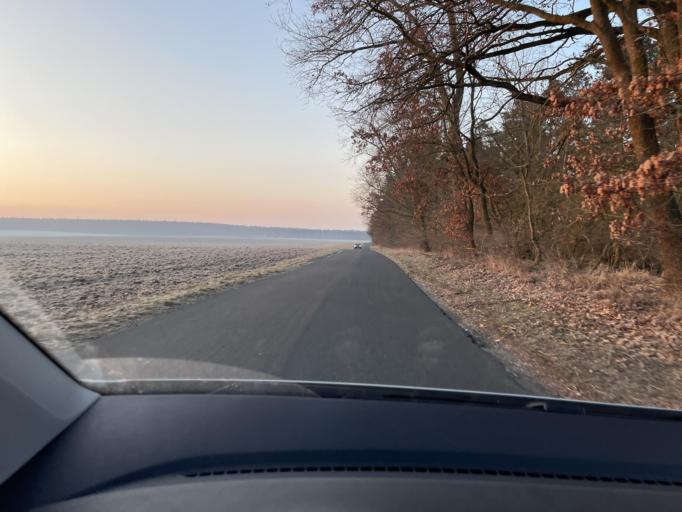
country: DE
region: Brandenburg
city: Roskow
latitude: 52.4054
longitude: 12.6924
